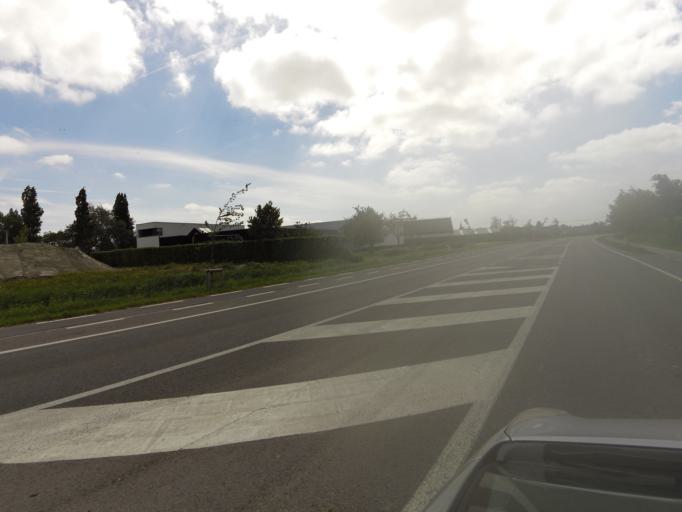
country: BE
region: Flanders
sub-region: Provincie West-Vlaanderen
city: Diksmuide
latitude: 51.0869
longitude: 2.8839
